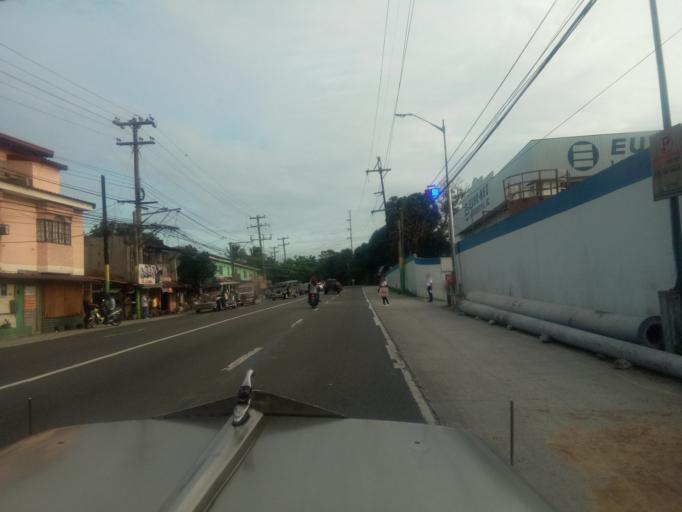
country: PH
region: Calabarzon
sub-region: Province of Cavite
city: Biga
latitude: 14.2857
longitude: 120.9595
